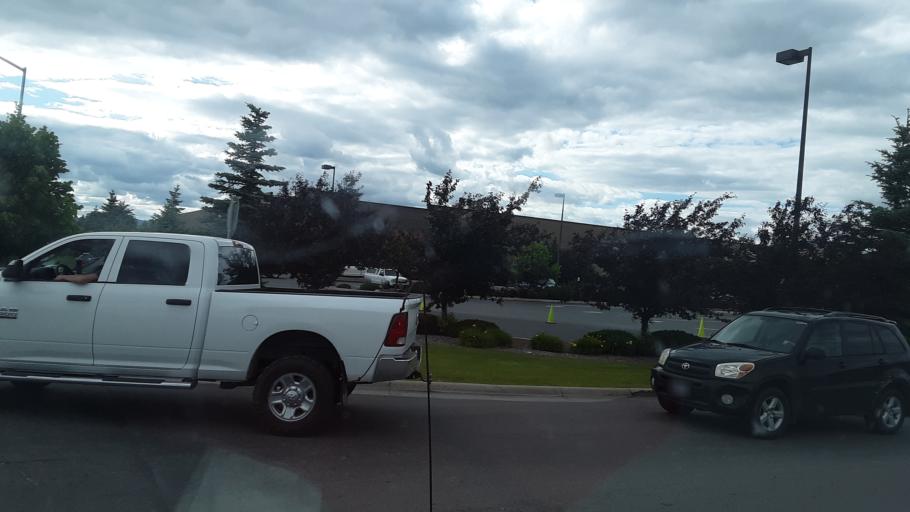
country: US
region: Montana
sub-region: Flathead County
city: Kalispell
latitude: 48.2333
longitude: -114.3315
